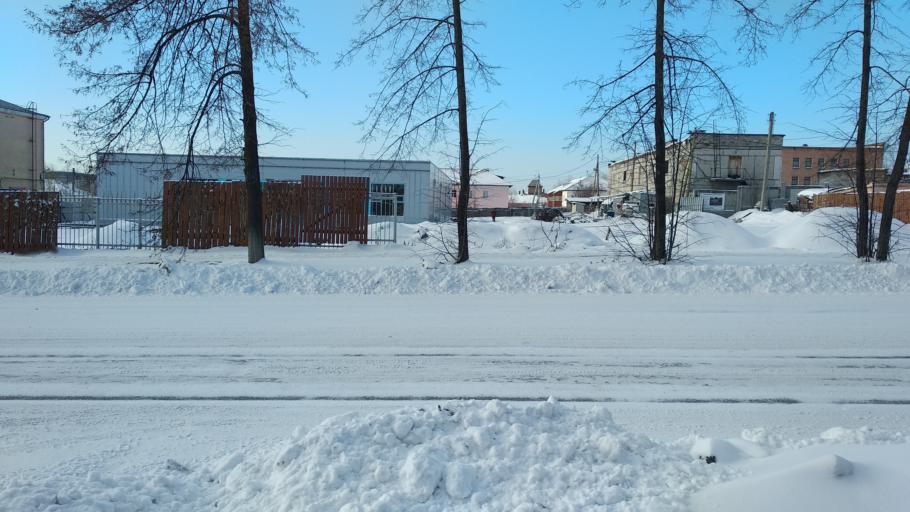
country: RU
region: Sverdlovsk
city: Krasnotur'insk
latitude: 59.7655
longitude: 60.1806
